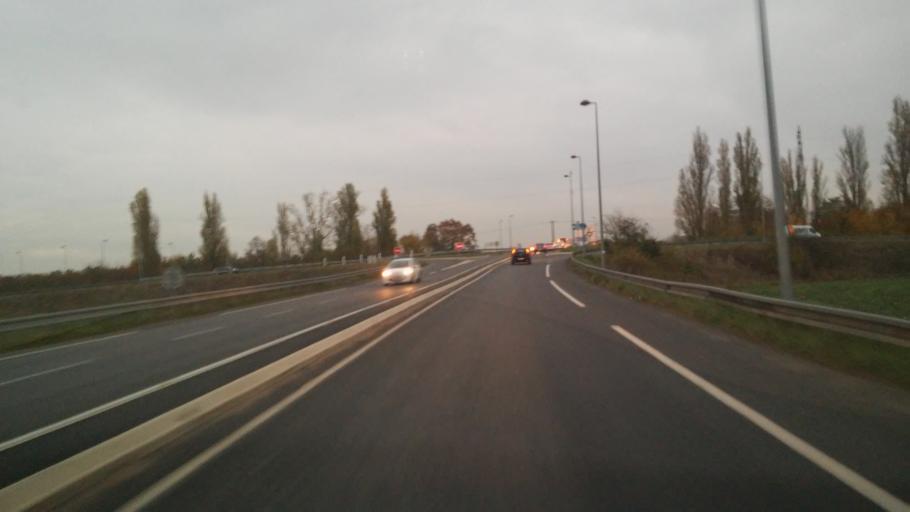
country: FR
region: Lorraine
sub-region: Departement de la Moselle
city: Talange
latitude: 49.2415
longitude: 6.1779
